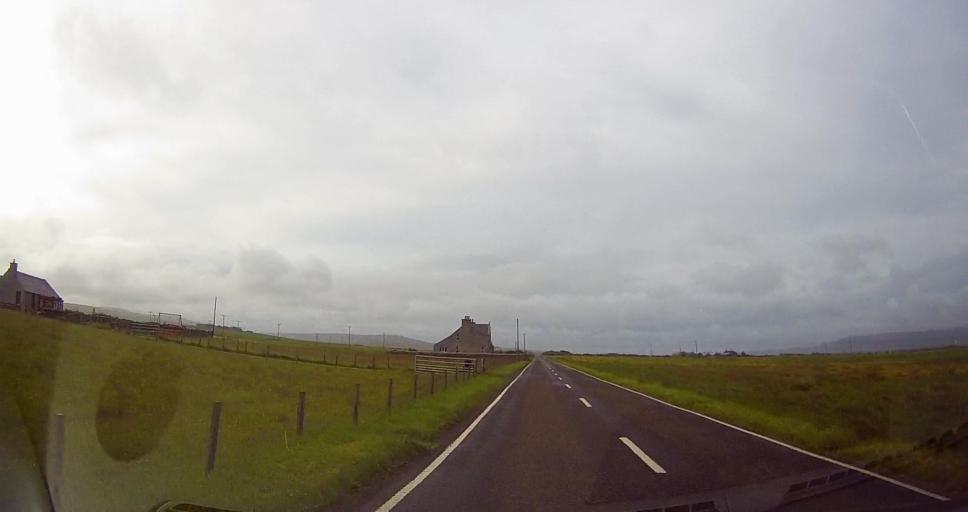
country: GB
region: Scotland
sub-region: Orkney Islands
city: Stromness
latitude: 58.9819
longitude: -3.2465
